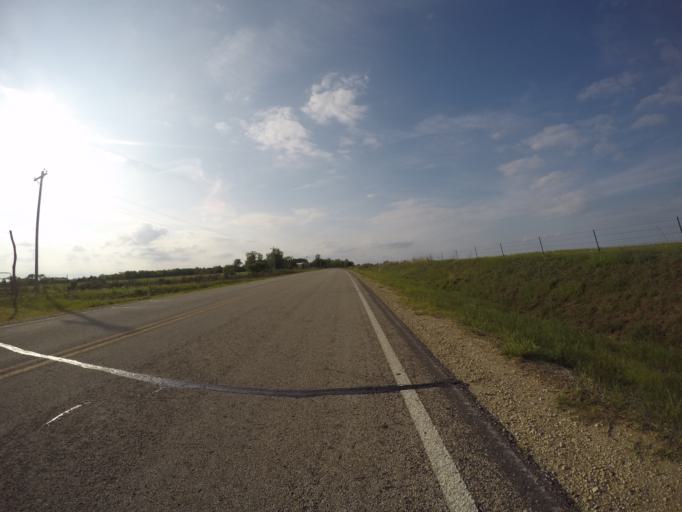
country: US
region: Kansas
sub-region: Pottawatomie County
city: Westmoreland
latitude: 39.4046
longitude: -96.6059
